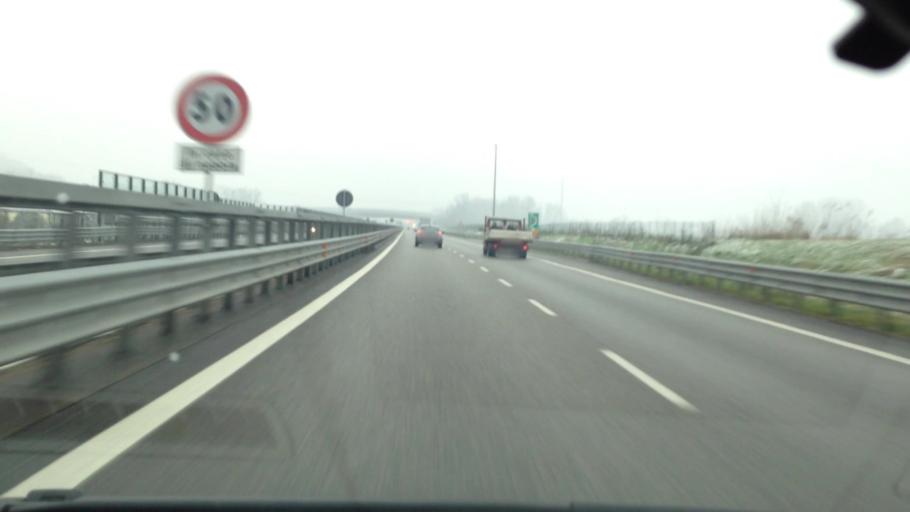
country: IT
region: Piedmont
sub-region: Provincia di Asti
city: Mongardino
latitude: 44.8605
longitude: 8.2028
